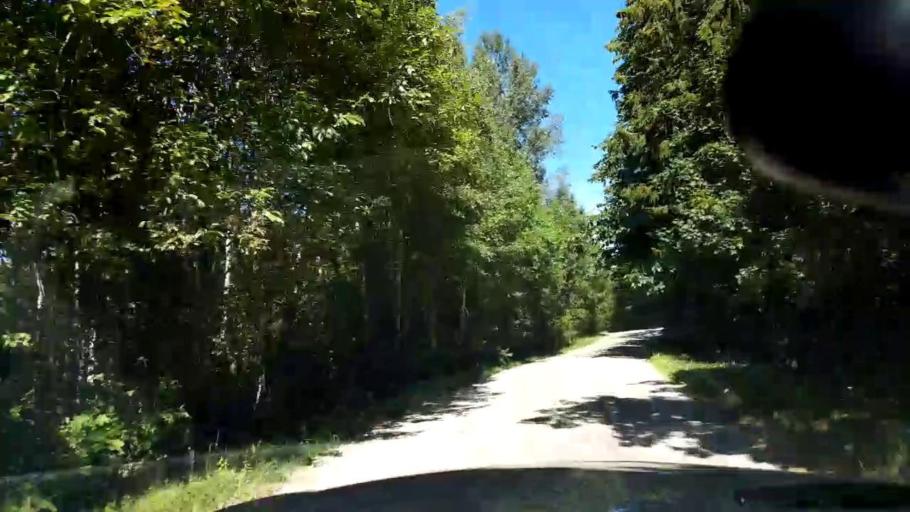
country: SE
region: Uppsala
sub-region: Habo Kommun
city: Balsta
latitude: 59.6165
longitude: 17.6140
